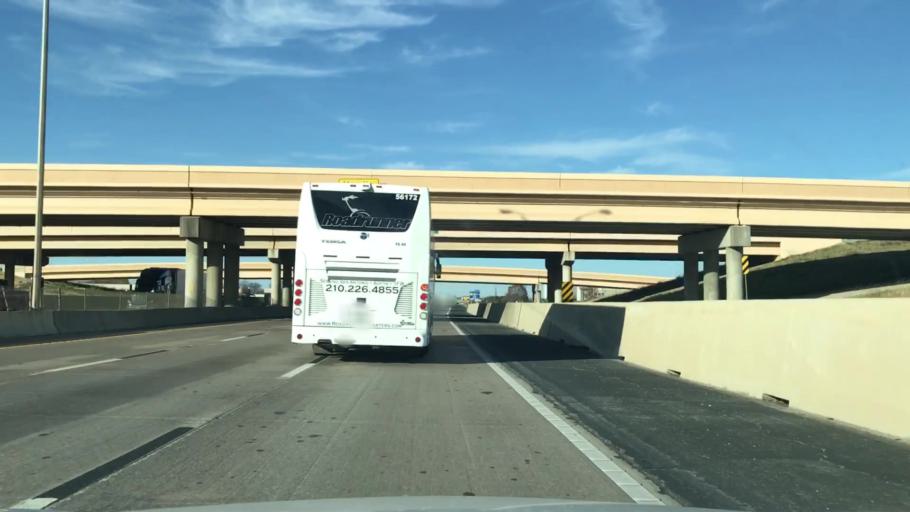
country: US
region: Texas
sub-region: Johnson County
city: Burleson
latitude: 32.5773
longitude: -97.3195
